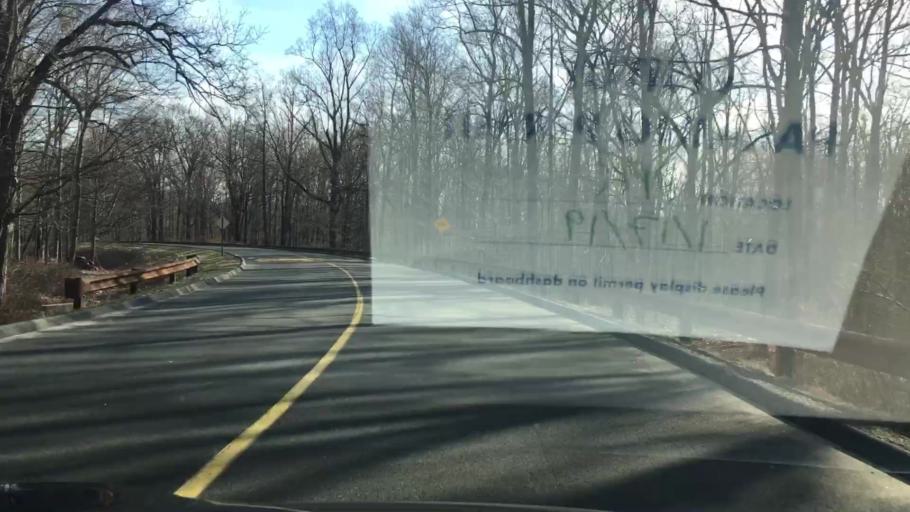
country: US
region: New York
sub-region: Putnam County
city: Peach Lake
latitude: 41.3741
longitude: -73.5229
